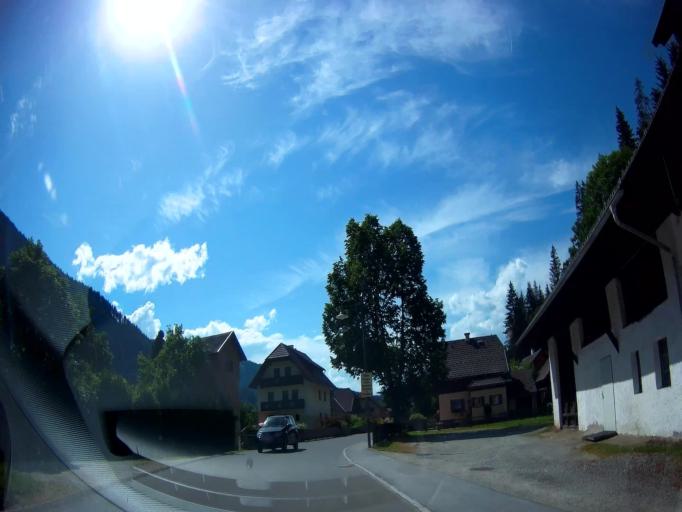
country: AT
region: Salzburg
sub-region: Politischer Bezirk Tamsweg
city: Thomatal
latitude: 47.0726
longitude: 13.7478
